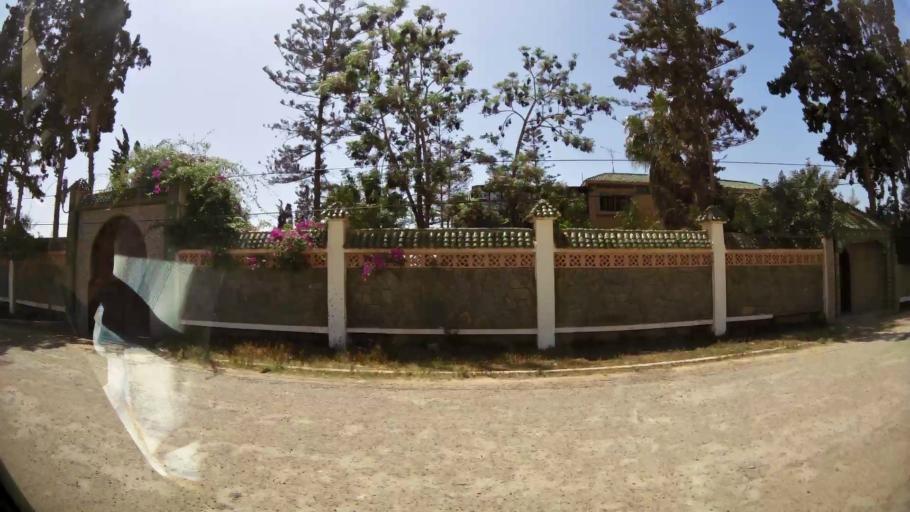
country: MA
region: Souss-Massa-Draa
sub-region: Inezgane-Ait Mellou
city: Inezgane
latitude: 30.3453
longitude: -9.5141
